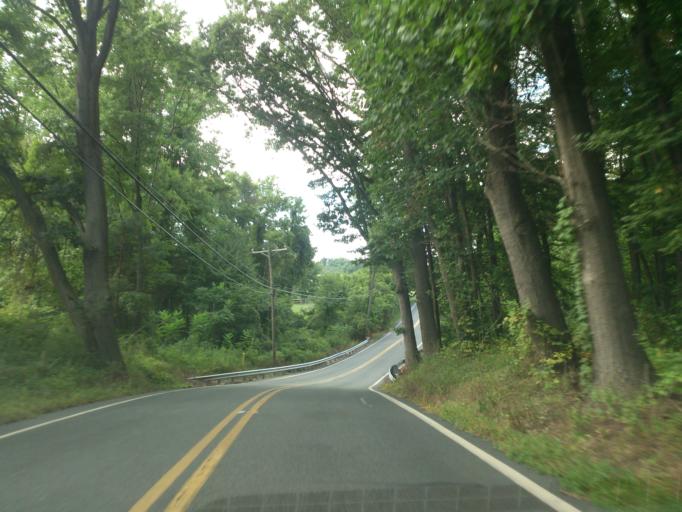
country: US
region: Pennsylvania
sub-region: Lebanon County
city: Campbelltown
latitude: 40.2550
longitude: -76.5864
